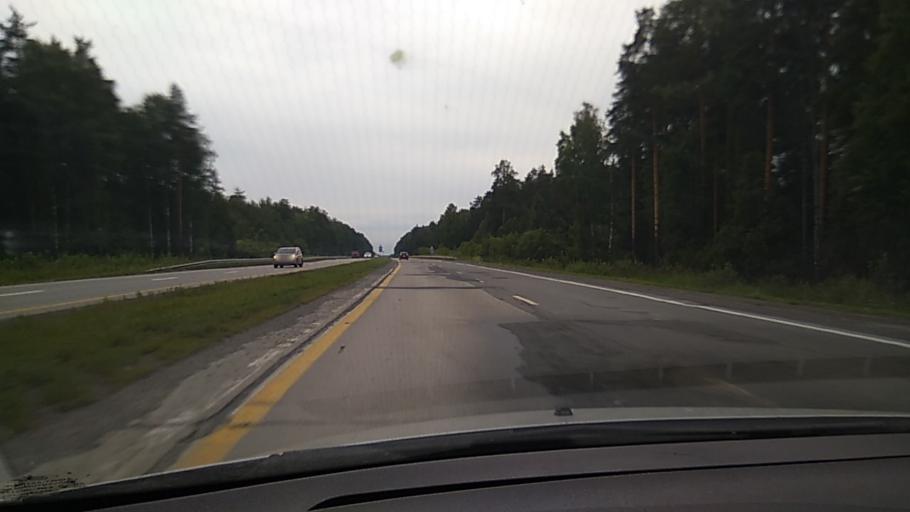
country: RU
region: Sverdlovsk
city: Sysert'
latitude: 56.4454
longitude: 60.8763
